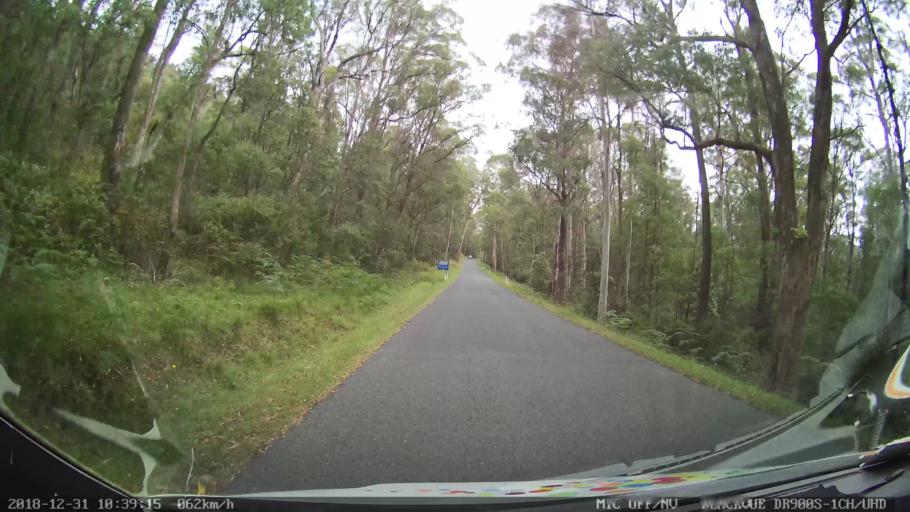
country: AU
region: New South Wales
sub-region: Snowy River
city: Jindabyne
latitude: -36.4010
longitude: 148.1770
